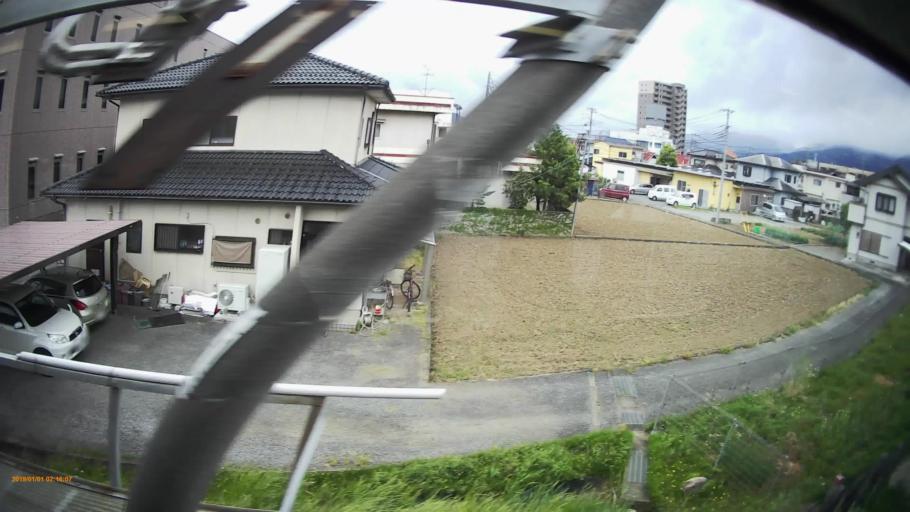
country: JP
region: Yamanashi
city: Kofu-shi
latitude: 35.6697
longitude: 138.5582
